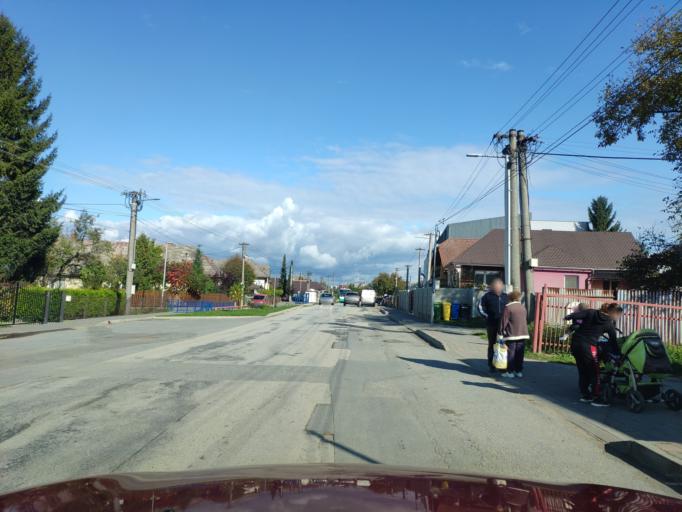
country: SK
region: Presovsky
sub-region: Okres Presov
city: Presov
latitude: 48.9216
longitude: 21.2604
